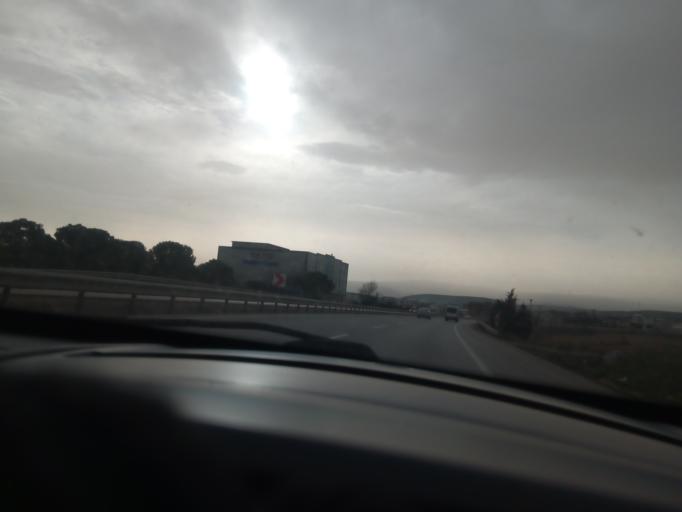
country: TR
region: Bursa
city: Tatkavakli
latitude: 40.0451
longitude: 28.3769
